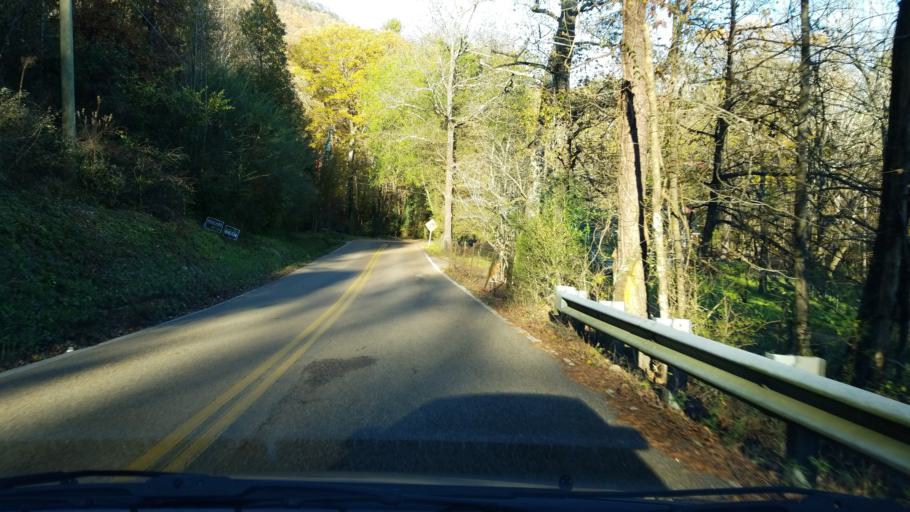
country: US
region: Tennessee
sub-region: Hamilton County
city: Falling Water
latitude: 35.2071
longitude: -85.2573
